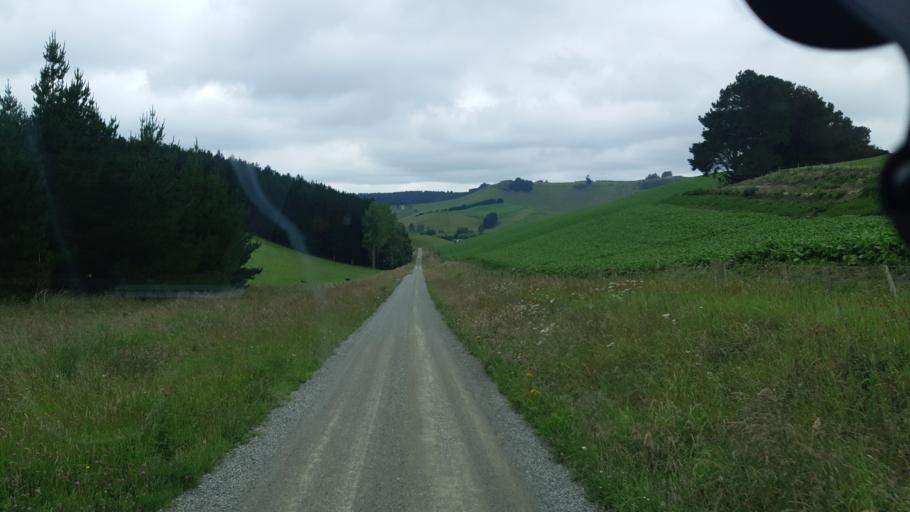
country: NZ
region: Canterbury
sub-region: Timaru District
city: Pleasant Point
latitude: -44.3471
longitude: 171.0419
